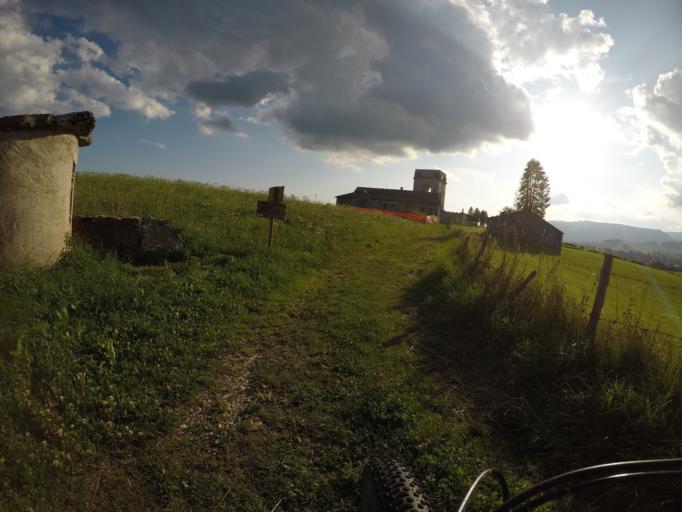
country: IT
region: Veneto
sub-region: Provincia di Vicenza
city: Asiago
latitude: 45.8755
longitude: 11.5243
